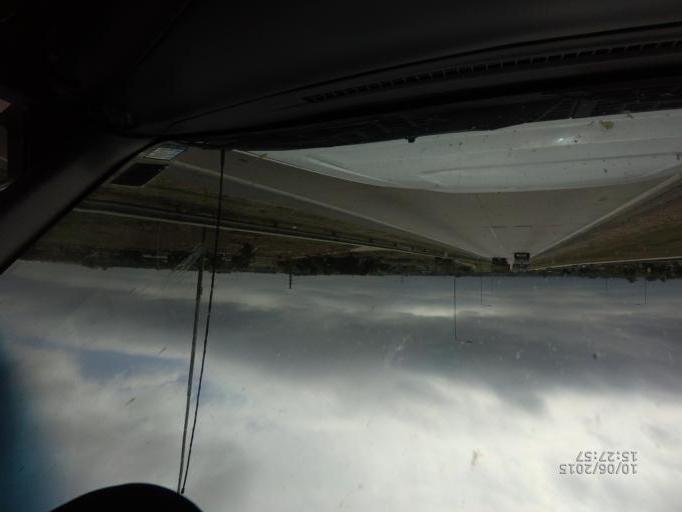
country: AR
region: Cordoba
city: Malvinas Argentinas
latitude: -31.4156
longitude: -64.1147
